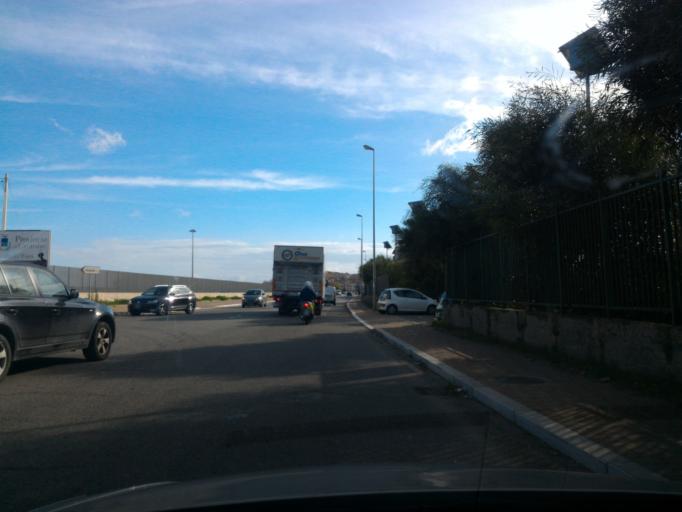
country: IT
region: Calabria
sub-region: Provincia di Crotone
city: Crotone
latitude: 39.0865
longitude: 17.1192
